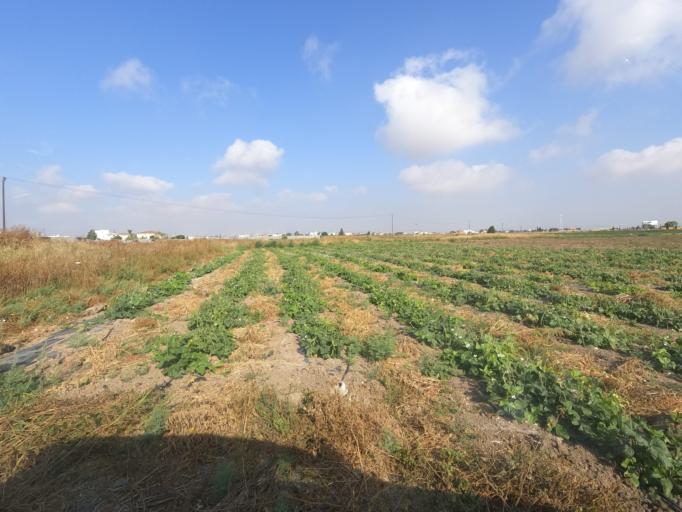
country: CY
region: Larnaka
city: Meneou
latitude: 34.8721
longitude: 33.6036
